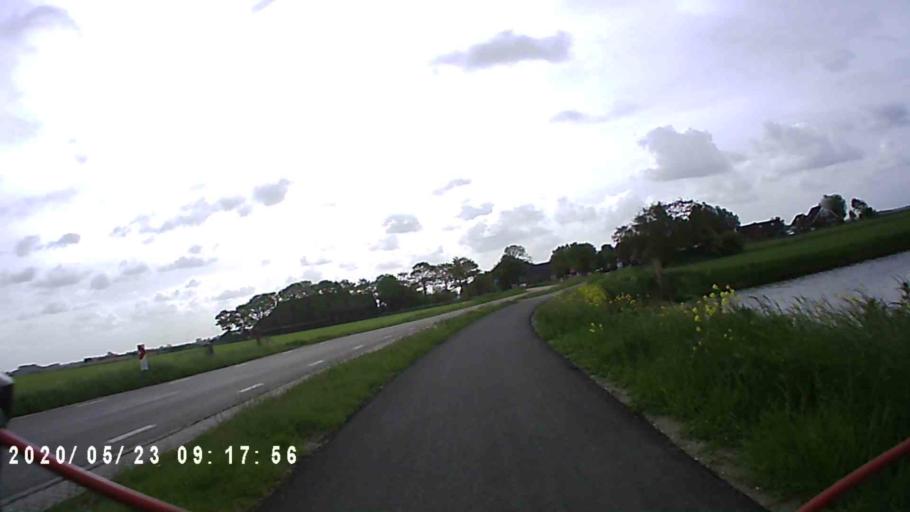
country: NL
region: Groningen
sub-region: Gemeente Bedum
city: Bedum
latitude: 53.3002
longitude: 6.6608
